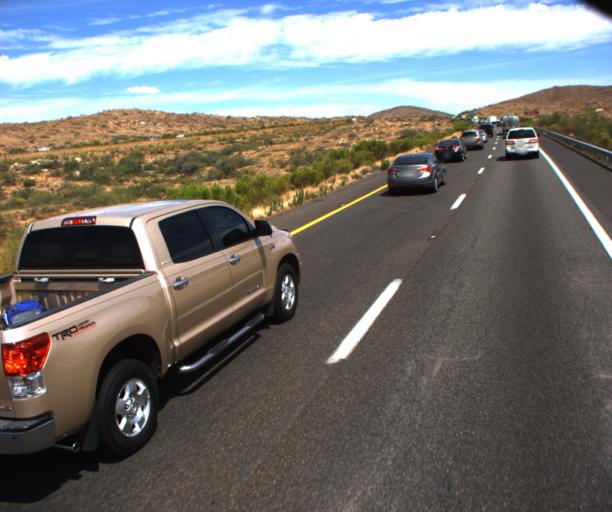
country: US
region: Arizona
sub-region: Yavapai County
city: Cordes Lakes
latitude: 34.2743
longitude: -112.1136
